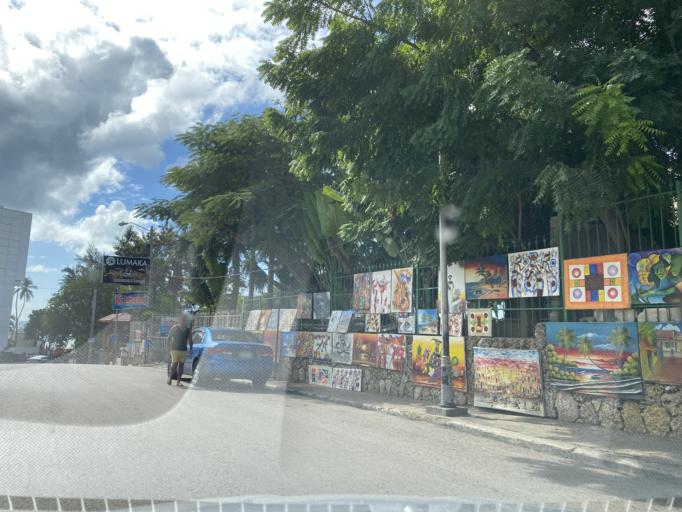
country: DO
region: Santo Domingo
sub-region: Santo Domingo
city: Boca Chica
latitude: 18.4494
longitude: -69.6056
